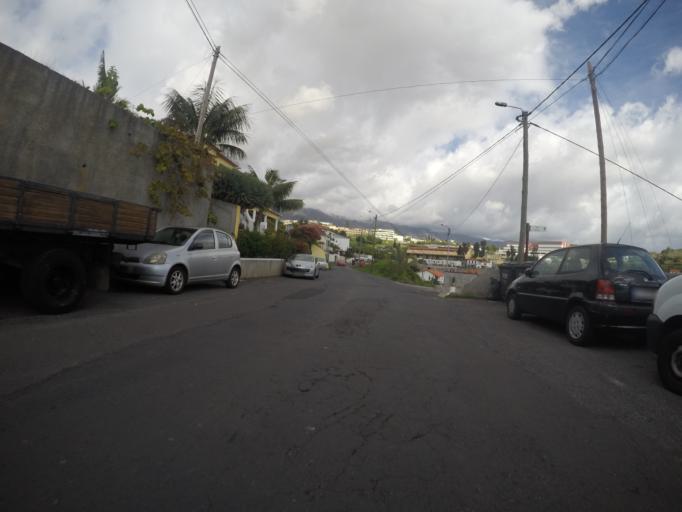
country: PT
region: Madeira
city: Camara de Lobos
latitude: 32.6497
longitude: -16.9483
